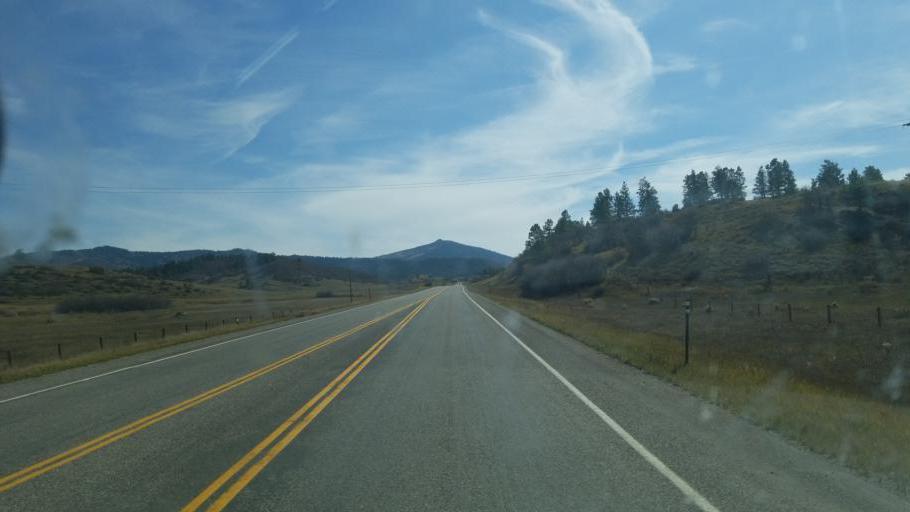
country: US
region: New Mexico
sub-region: Rio Arriba County
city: Dulce
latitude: 37.0131
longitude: -106.8048
